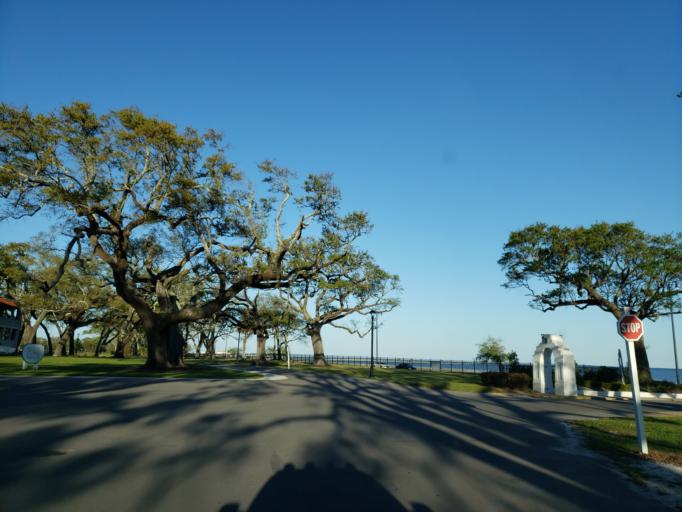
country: US
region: Mississippi
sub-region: Harrison County
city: Gulfport
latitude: 30.3769
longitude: -89.0522
